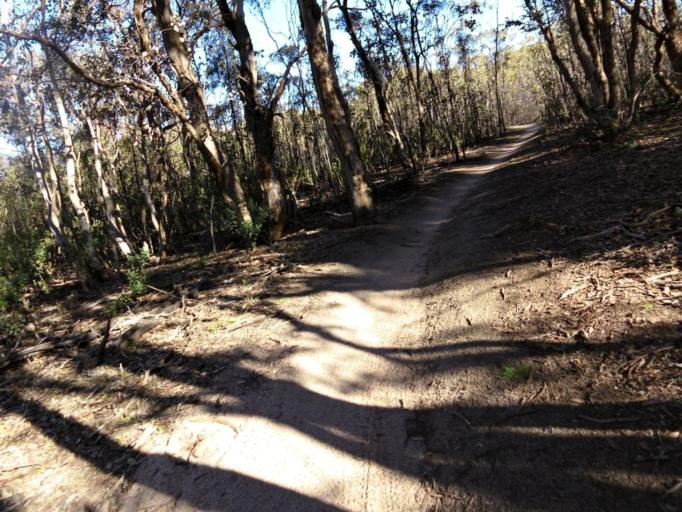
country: AU
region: Victoria
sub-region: Wyndham
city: Little River
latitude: -37.9280
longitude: 144.4457
